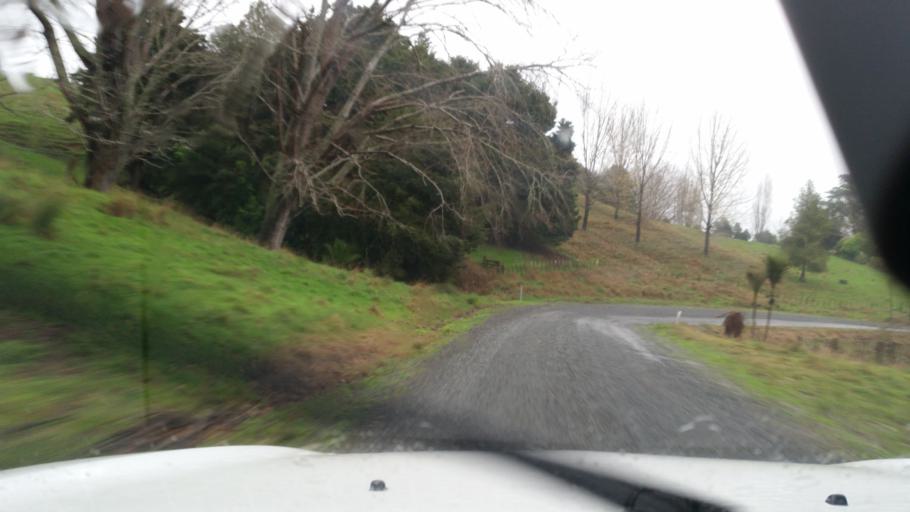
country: NZ
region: Northland
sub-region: Kaipara District
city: Dargaville
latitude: -35.7370
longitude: 173.9592
